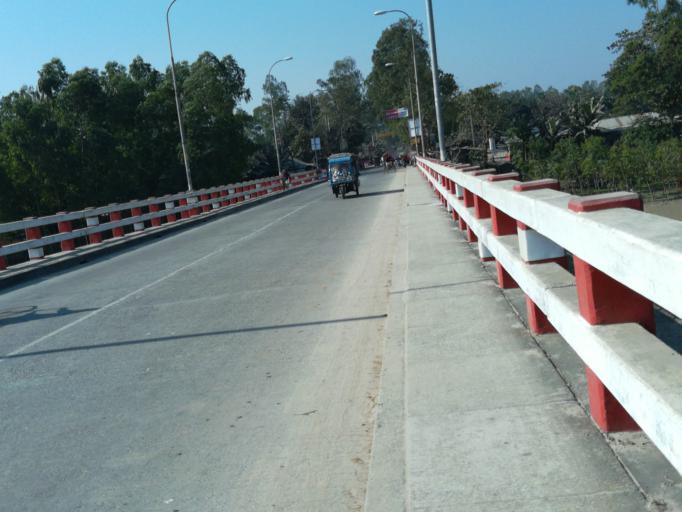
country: BD
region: Rangpur Division
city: Nageswari
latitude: 25.8187
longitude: 89.6662
